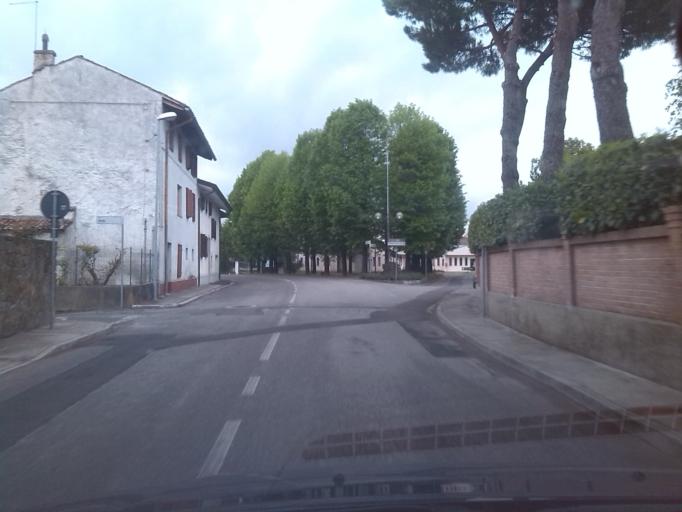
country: IT
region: Friuli Venezia Giulia
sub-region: Provincia di Gorizia
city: San Lorenzo Isontino
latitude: 45.9319
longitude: 13.5260
